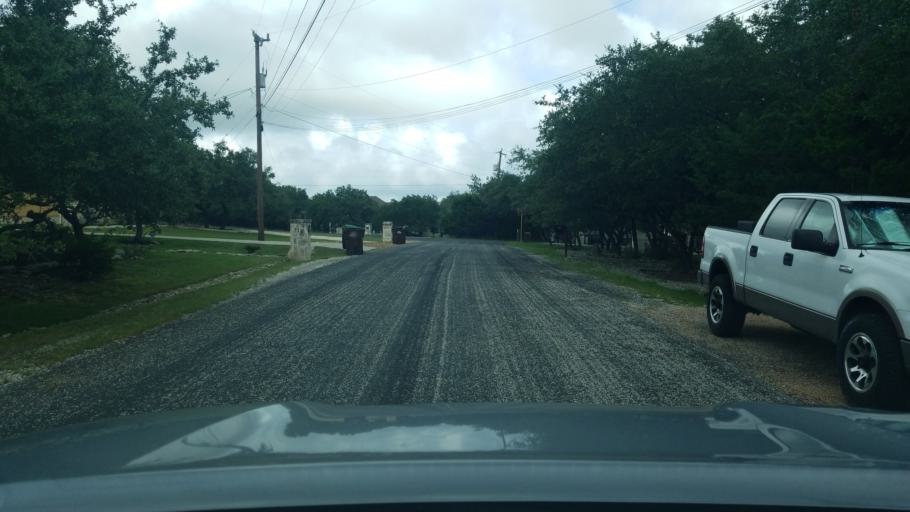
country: US
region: Texas
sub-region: Bexar County
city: Timberwood Park
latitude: 29.6894
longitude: -98.4970
